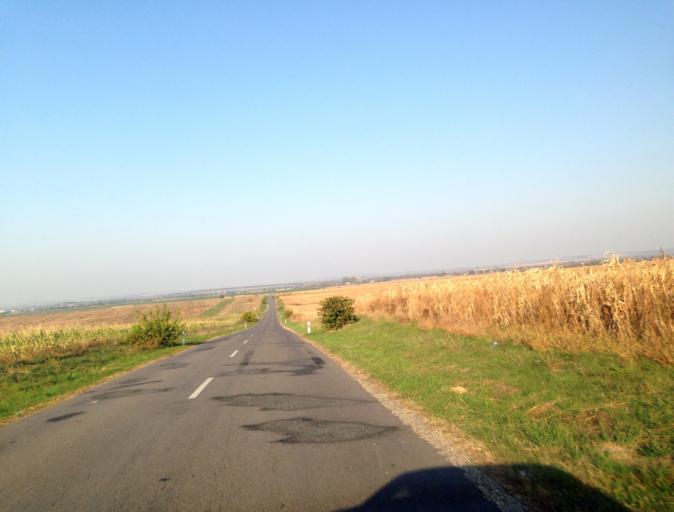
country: SK
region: Nitriansky
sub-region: Okres Komarno
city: Hurbanovo
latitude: 47.9023
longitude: 18.2785
